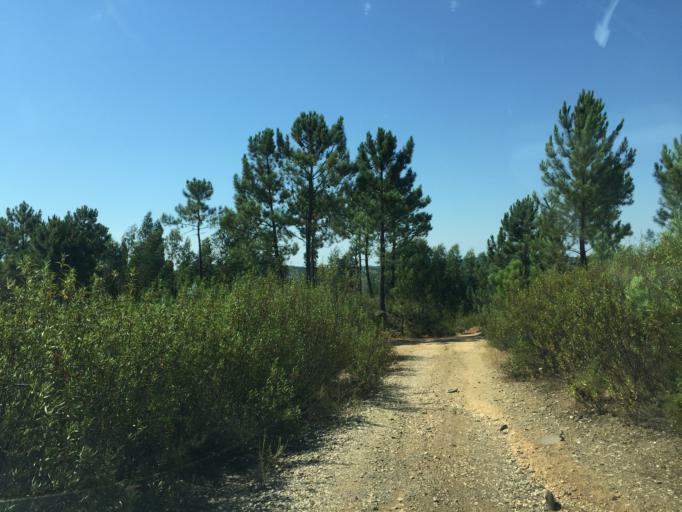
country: PT
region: Santarem
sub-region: Ferreira do Zezere
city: Ferreira do Zezere
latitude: 39.5799
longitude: -8.2769
